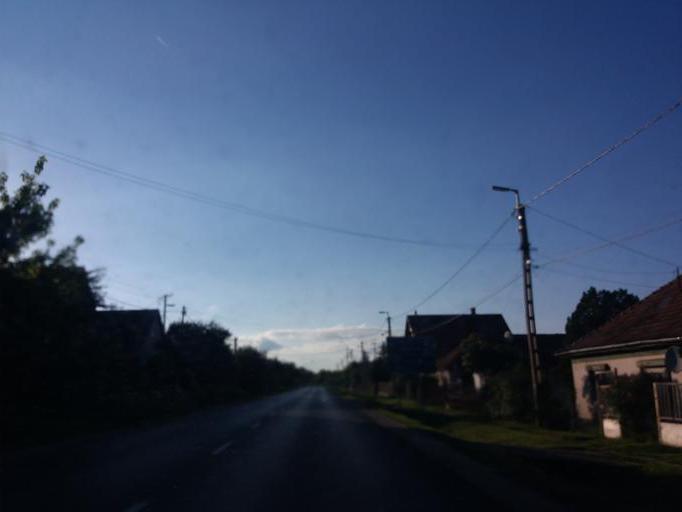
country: HU
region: Fejer
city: Martonvasar
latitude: 47.3266
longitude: 18.7799
